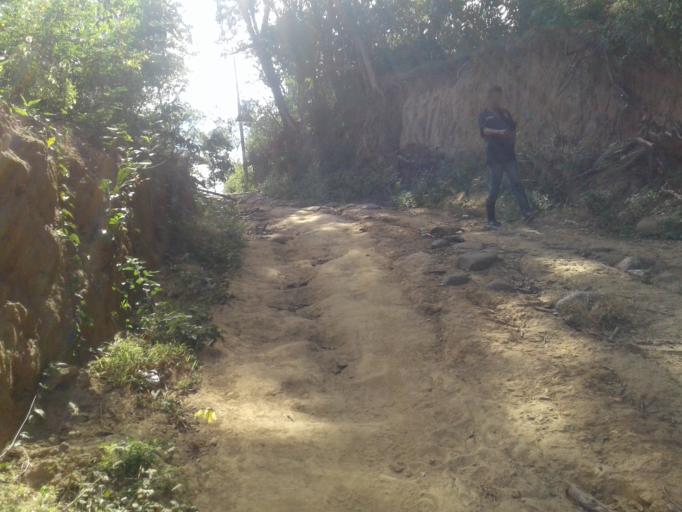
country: NI
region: Carazo
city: Santa Teresa
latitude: 11.6284
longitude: -86.1911
